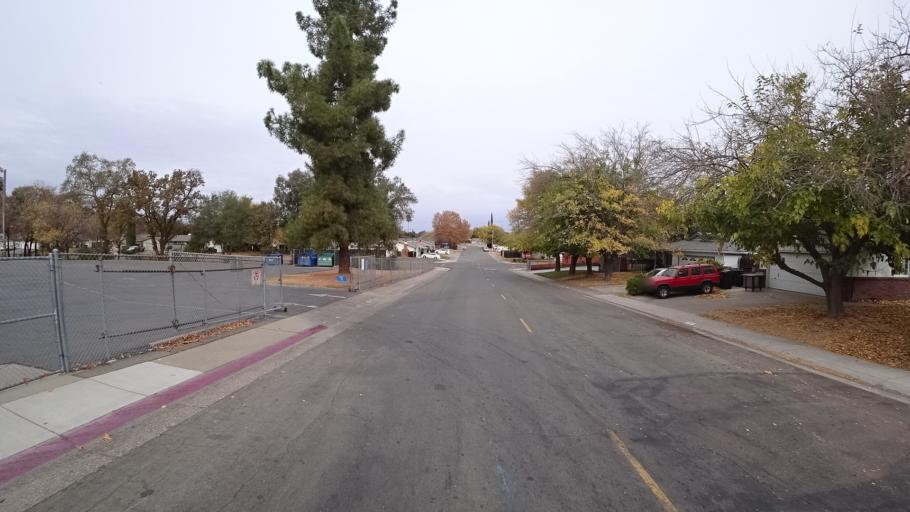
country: US
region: California
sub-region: Sacramento County
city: Citrus Heights
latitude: 38.7114
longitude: -121.3004
